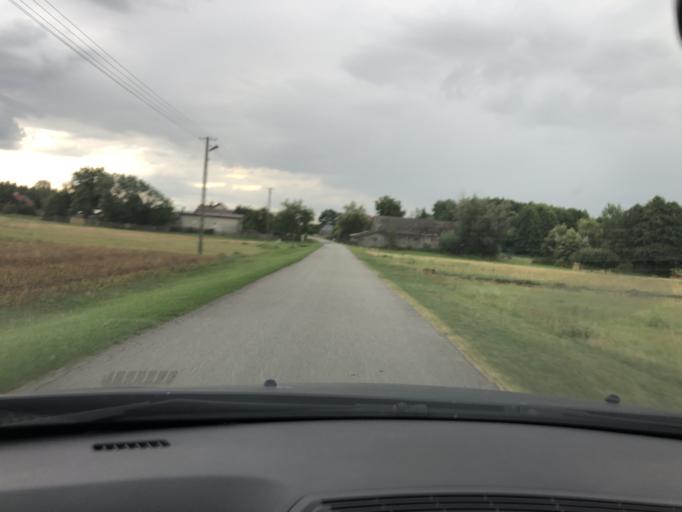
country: PL
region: Lodz Voivodeship
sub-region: Powiat wieruszowski
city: Czastary
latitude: 51.2423
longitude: 18.2798
